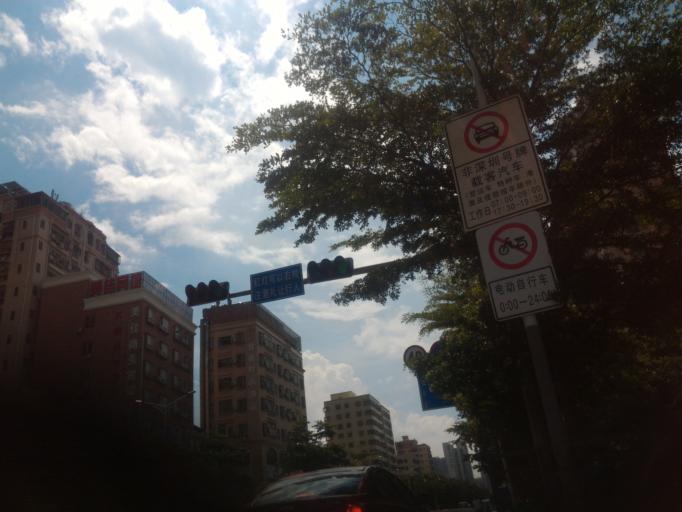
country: CN
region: Guangdong
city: Xixiang
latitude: 22.5706
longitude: 113.8672
